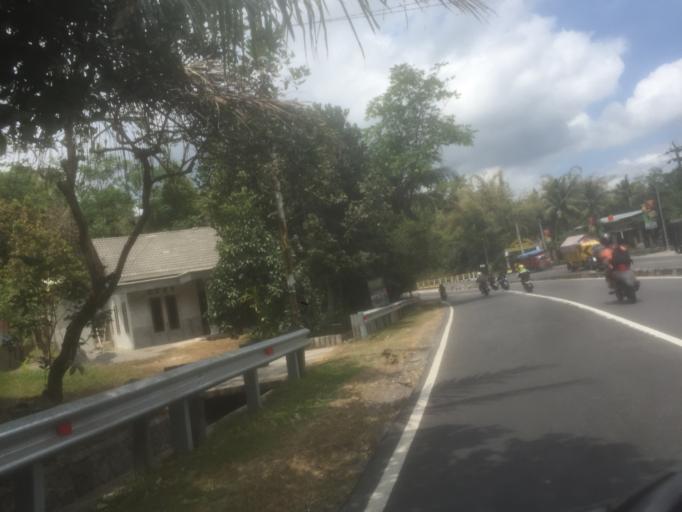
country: ID
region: Central Java
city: Muntilan
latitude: -7.6331
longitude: 110.3194
